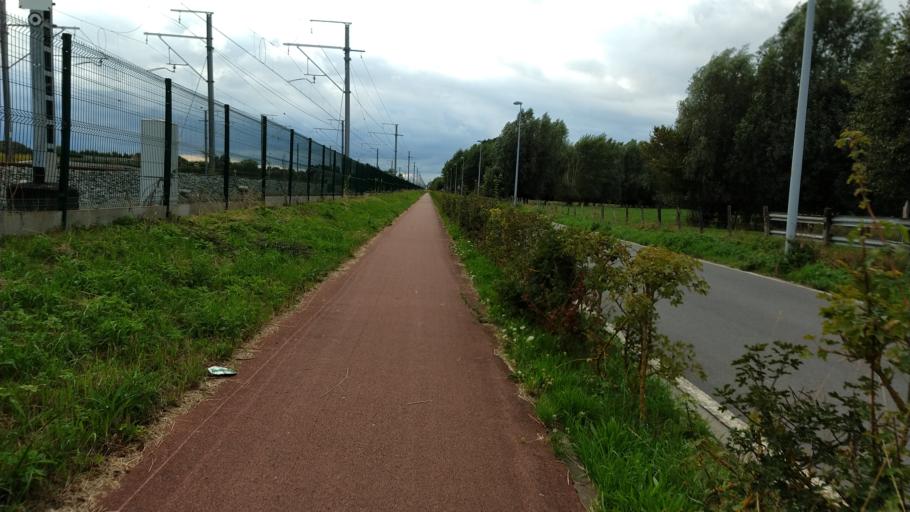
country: BE
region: Flanders
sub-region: Provincie Oost-Vlaanderen
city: Lovendegem
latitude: 51.0578
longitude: 3.6075
